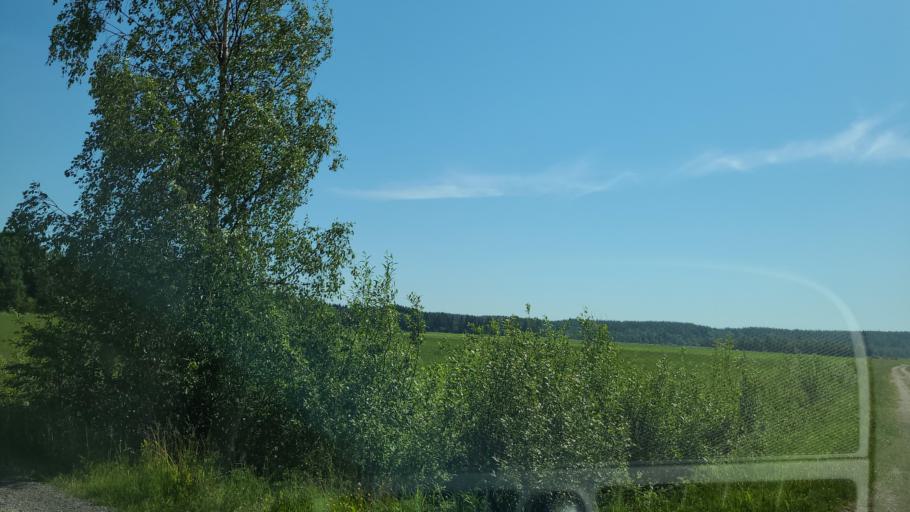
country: SE
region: Vaesterbotten
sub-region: Robertsfors Kommun
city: Robertsfors
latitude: 64.0865
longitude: 20.8529
